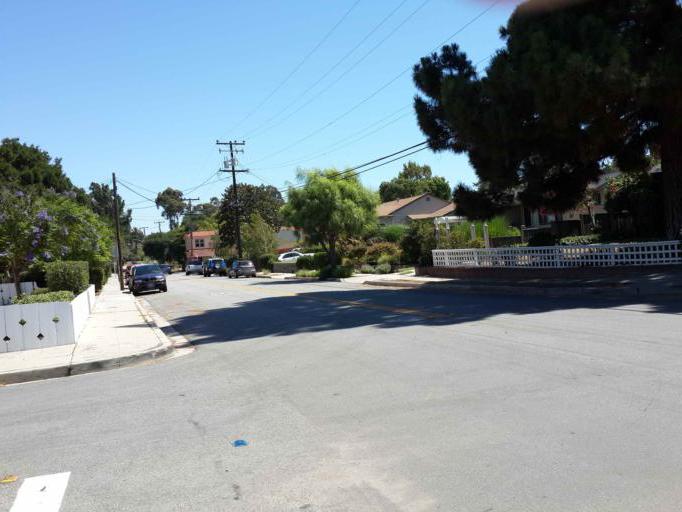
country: US
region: California
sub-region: San Luis Obispo County
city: San Luis Obispo
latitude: 35.2855
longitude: -120.6693
